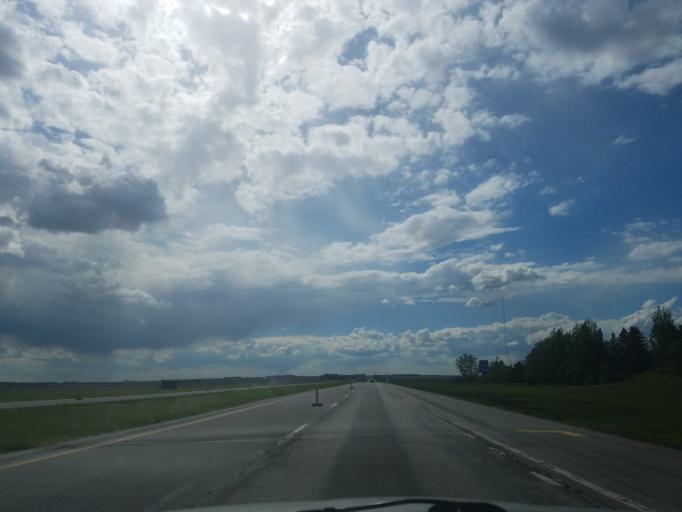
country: US
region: North Dakota
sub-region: Barnes County
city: Valley City
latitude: 46.9202
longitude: -97.7966
